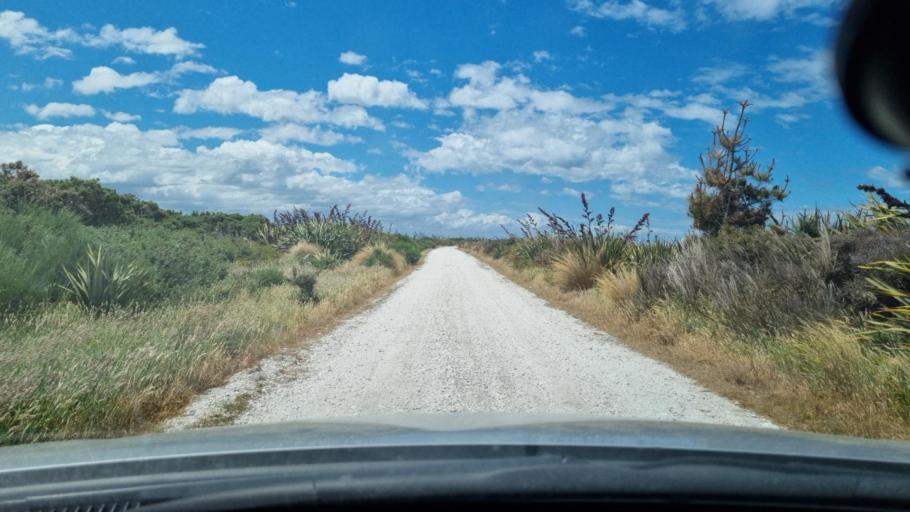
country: NZ
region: Southland
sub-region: Invercargill City
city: Bluff
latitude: -46.5732
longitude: 168.4985
